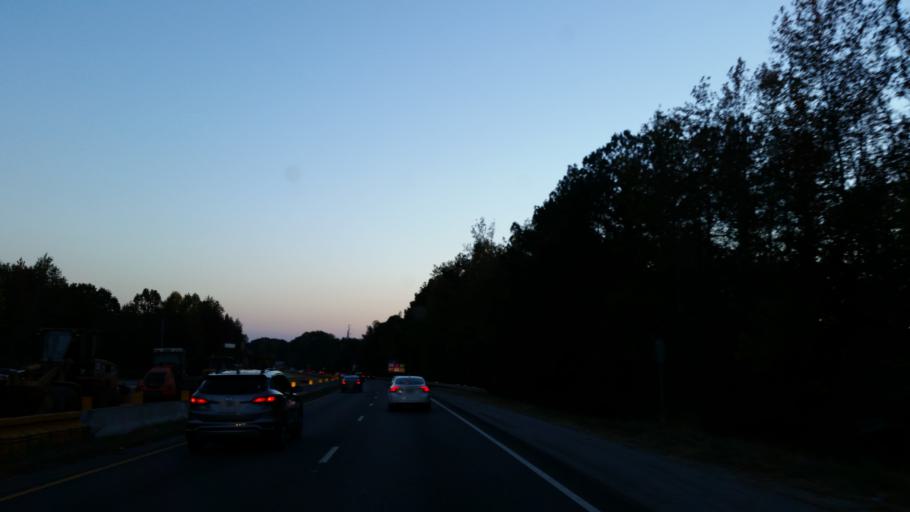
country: US
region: Georgia
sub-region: Forsyth County
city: Cumming
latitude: 34.2615
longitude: -84.0889
